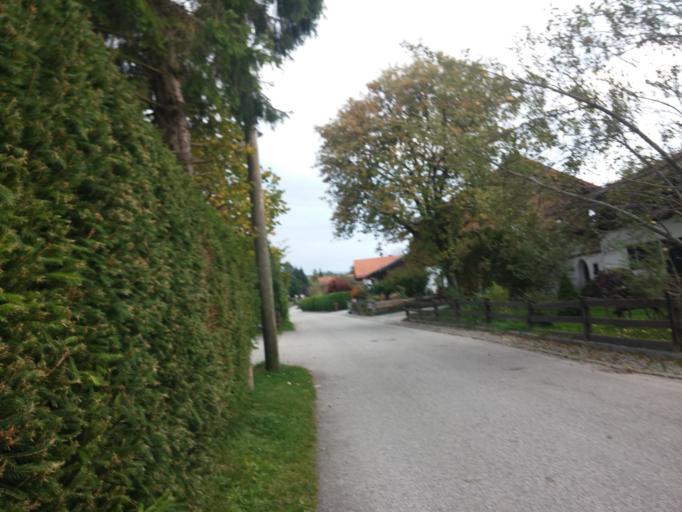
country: DE
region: Bavaria
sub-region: Upper Bavaria
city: Dietramszell
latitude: 47.8558
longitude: 11.5921
